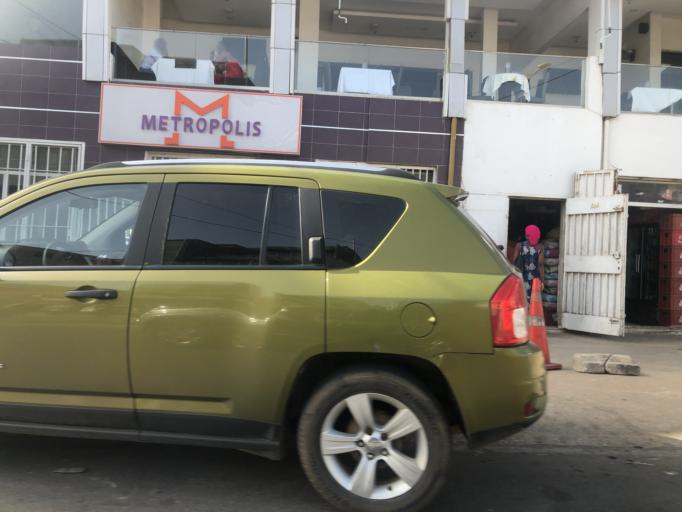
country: SN
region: Dakar
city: Mermoz Boabab
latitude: 14.7487
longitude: -17.5071
